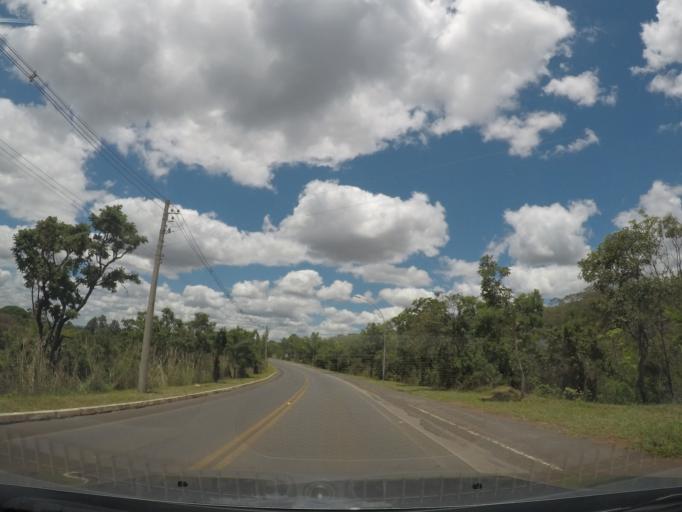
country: BR
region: Federal District
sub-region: Brasilia
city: Brasilia
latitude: -15.7843
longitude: -47.8053
